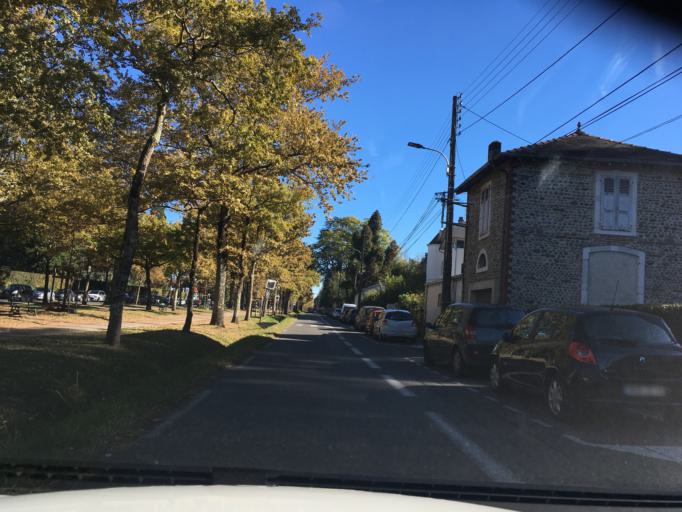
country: FR
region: Aquitaine
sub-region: Departement des Pyrenees-Atlantiques
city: Pau
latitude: 43.3035
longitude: -0.3508
